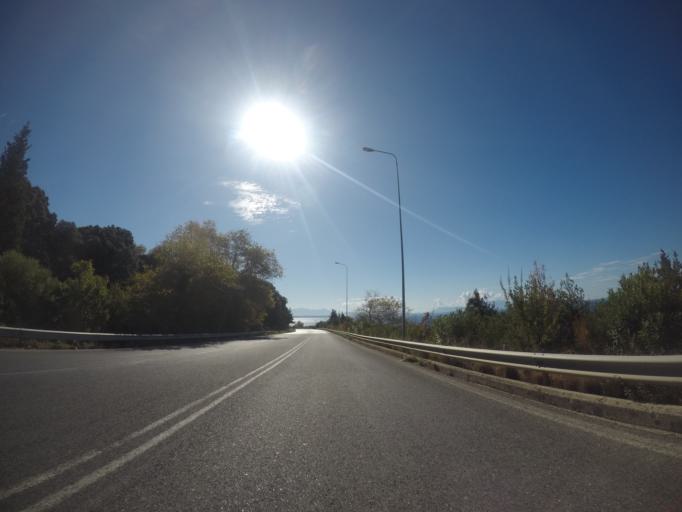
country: GR
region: Epirus
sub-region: Nomos Prevezis
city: Neos Oropos
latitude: 39.1054
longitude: 20.6370
